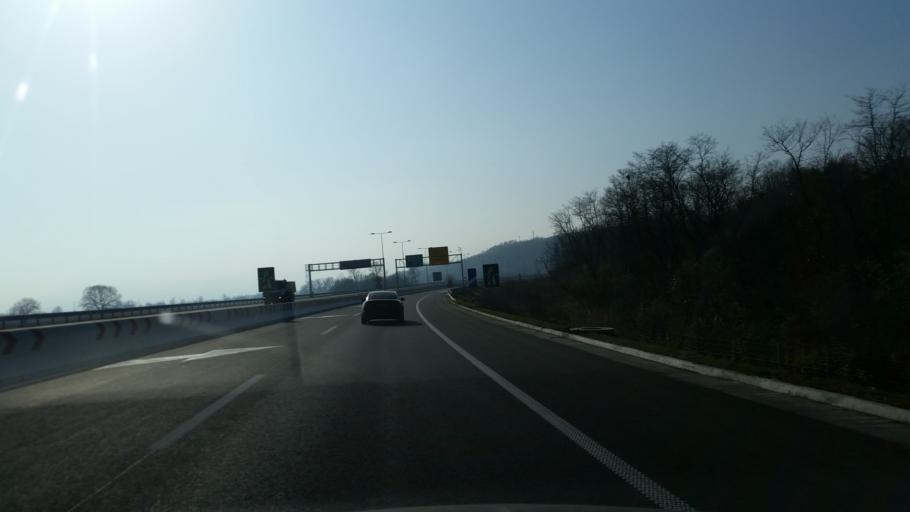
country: RS
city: Prislonica
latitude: 43.9262
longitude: 20.4010
